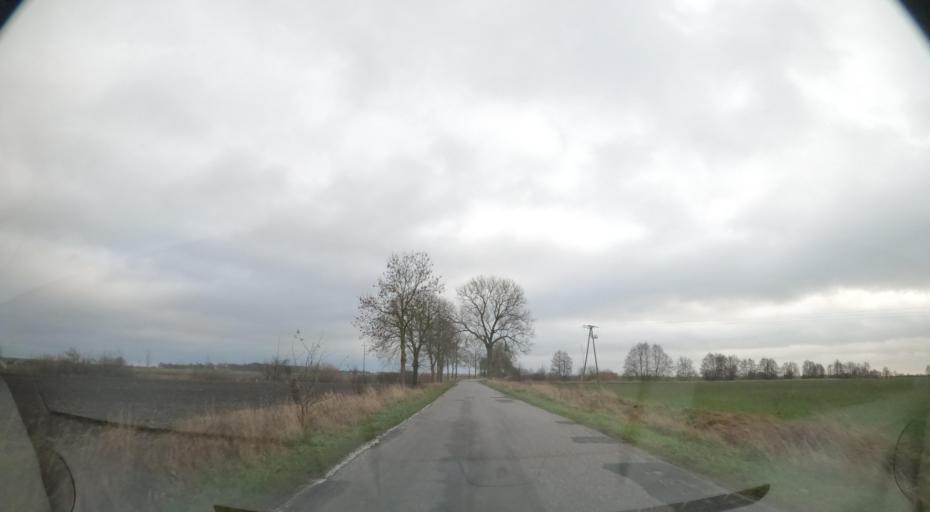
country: PL
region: Greater Poland Voivodeship
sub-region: Powiat pilski
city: Lobzenica
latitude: 53.2648
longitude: 17.2161
